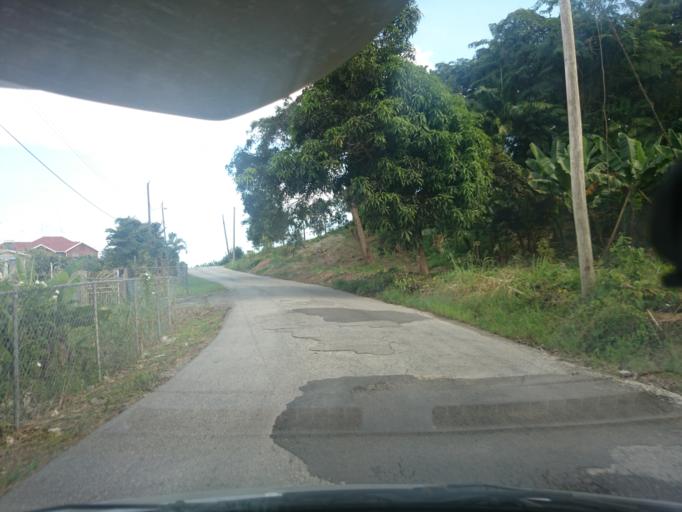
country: BB
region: Saint Joseph
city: Bathsheba
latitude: 13.2053
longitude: -59.5225
